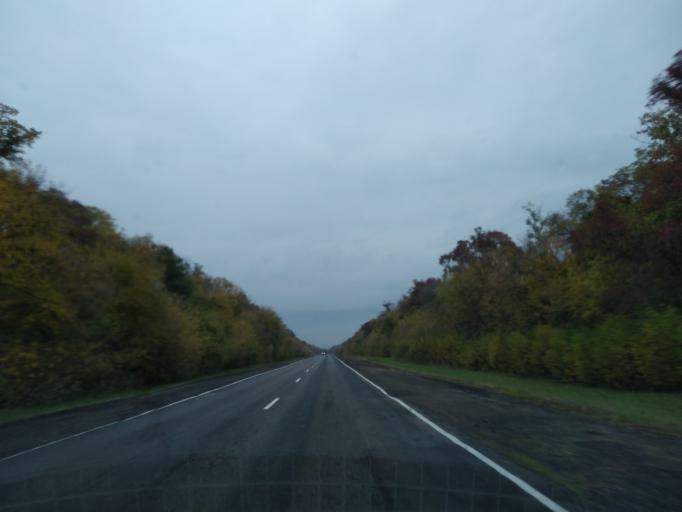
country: RU
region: Lipetsk
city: Zadonsk
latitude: 52.5063
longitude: 38.7576
